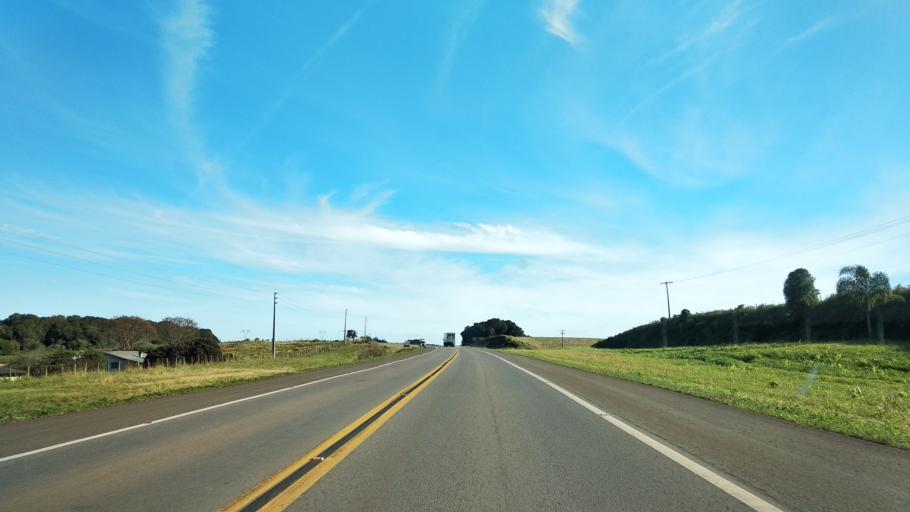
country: BR
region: Santa Catarina
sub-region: Celso Ramos
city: Celso Ramos
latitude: -27.4947
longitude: -51.3370
